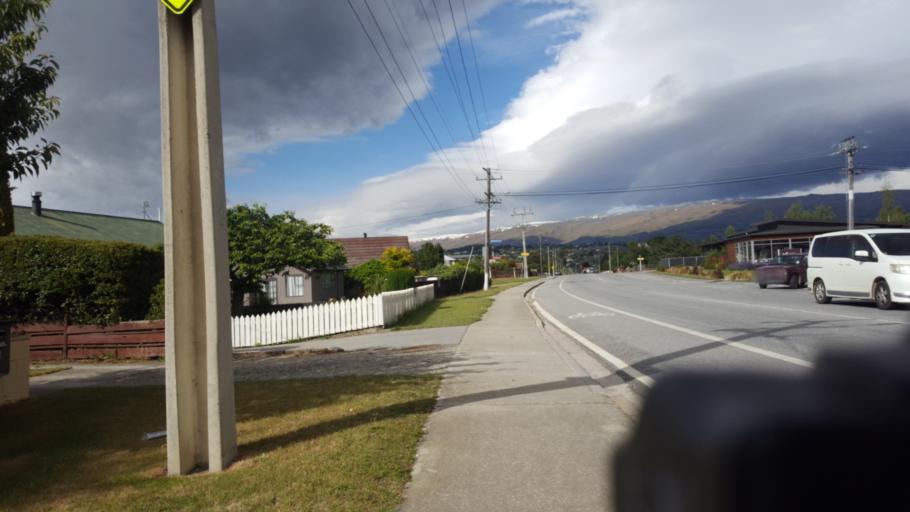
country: NZ
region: Otago
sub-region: Queenstown-Lakes District
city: Wanaka
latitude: -45.2484
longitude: 169.3998
